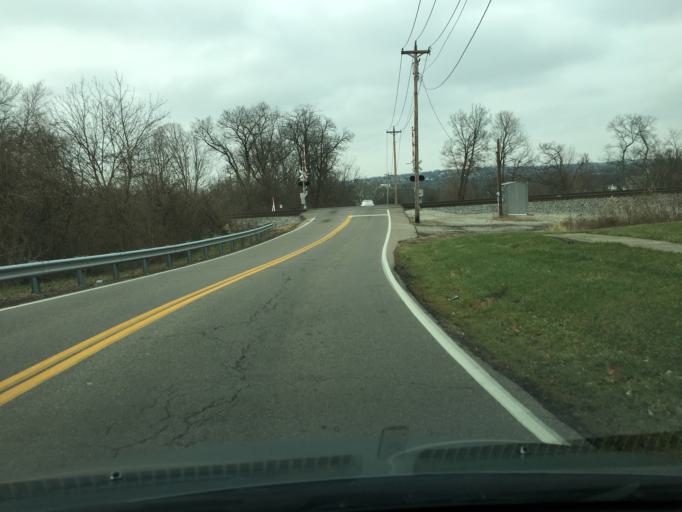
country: US
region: Ohio
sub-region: Butler County
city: Beckett Ridge
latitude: 39.3161
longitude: -84.4064
